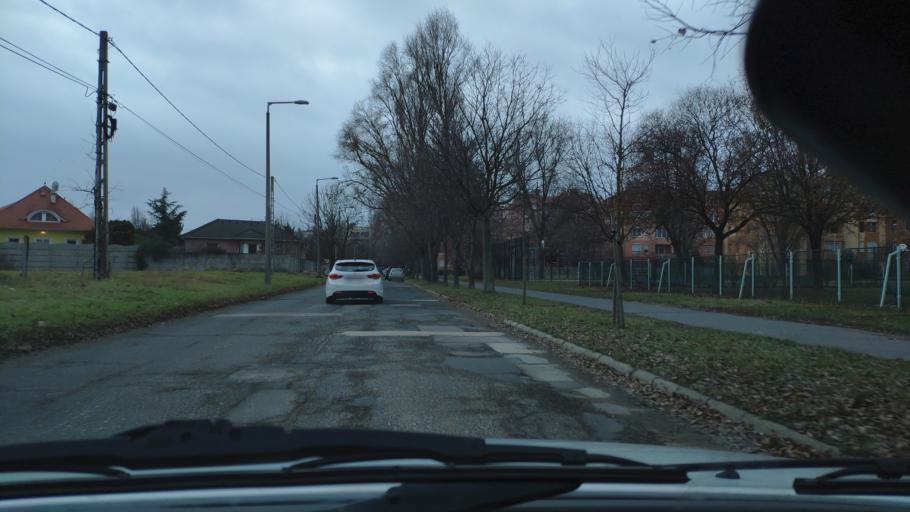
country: HU
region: Budapest
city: Budapest XXI. keruelet
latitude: 47.4043
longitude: 19.0778
